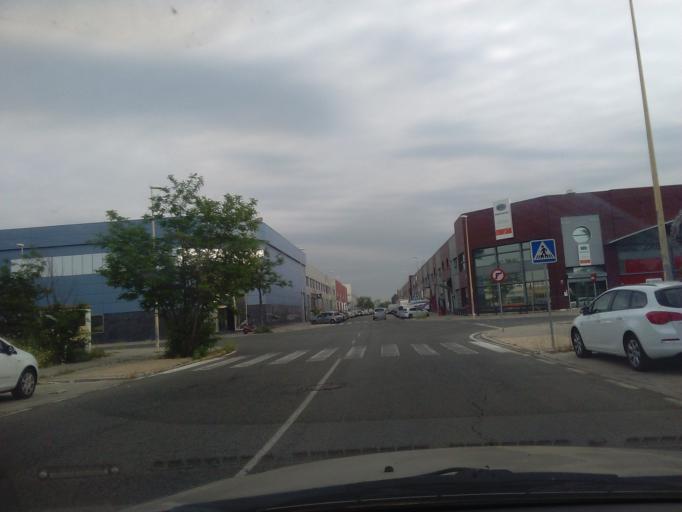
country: ES
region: Andalusia
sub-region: Provincia de Sevilla
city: Sevilla
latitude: 37.3798
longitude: -5.9303
